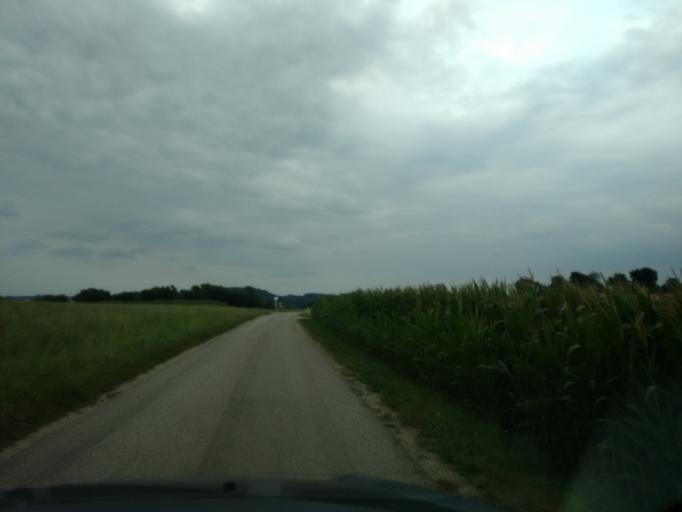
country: AT
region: Upper Austria
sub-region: Politischer Bezirk Grieskirchen
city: Bad Schallerbach
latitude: 48.2054
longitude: 13.9449
